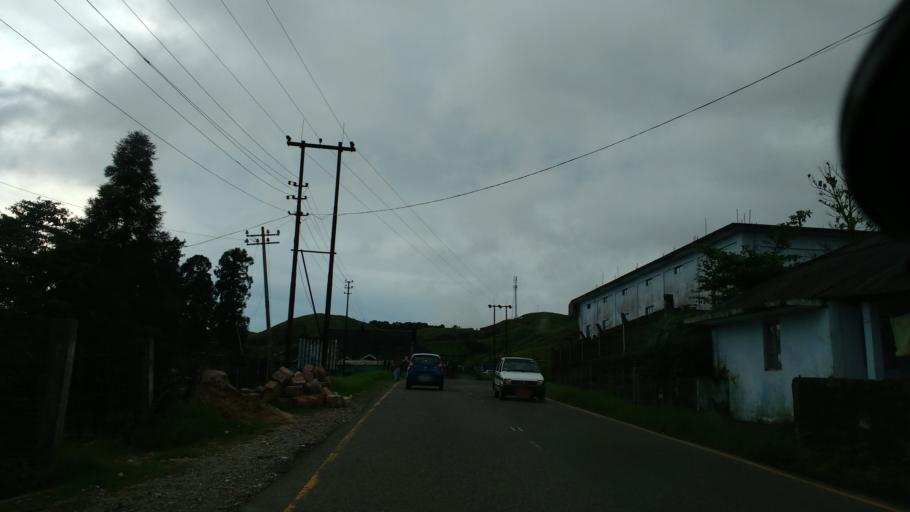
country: IN
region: Meghalaya
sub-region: East Khasi Hills
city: Cherrapunji
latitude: 25.2751
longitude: 91.7316
